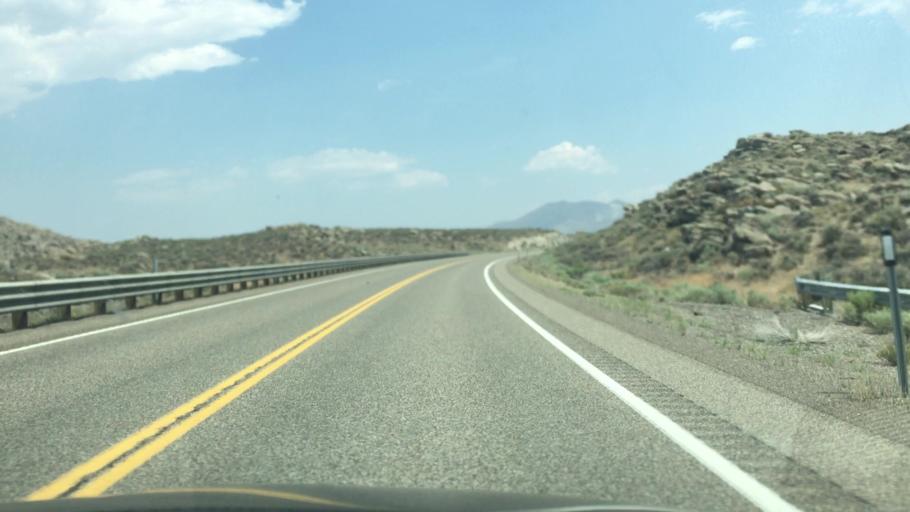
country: US
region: Nevada
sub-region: Elko County
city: Jackpot
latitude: 41.7364
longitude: -114.7874
